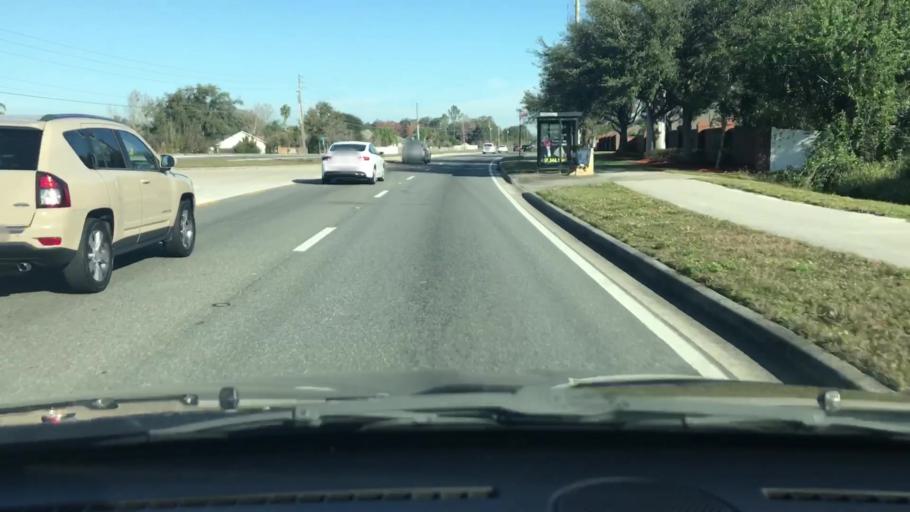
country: US
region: Florida
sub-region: Osceola County
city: Campbell
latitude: 28.2422
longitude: -81.4359
